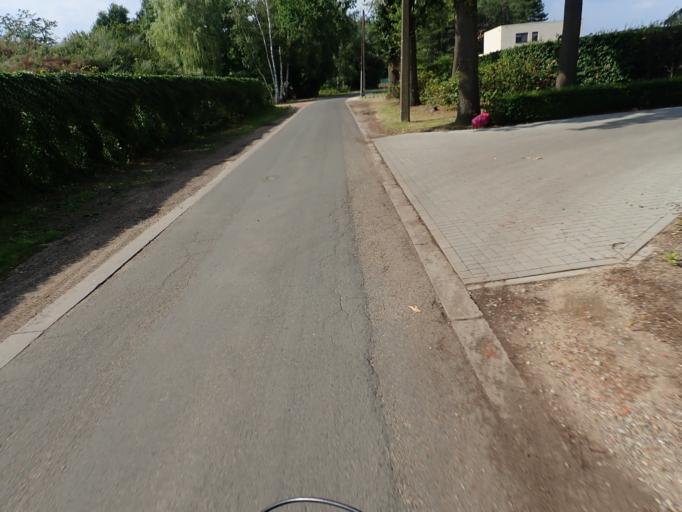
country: BE
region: Flanders
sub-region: Provincie Vlaams-Brabant
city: Keerbergen
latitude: 51.0176
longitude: 4.6311
